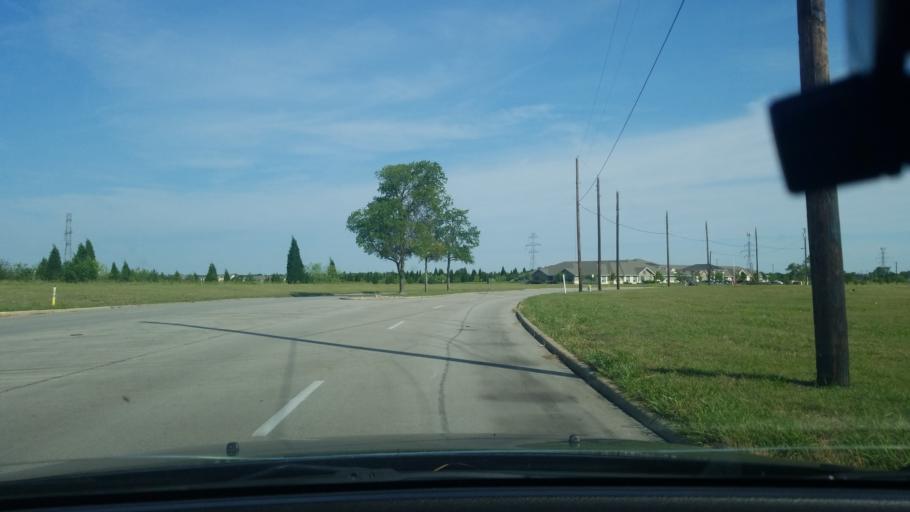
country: US
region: Texas
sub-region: Dallas County
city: Sunnyvale
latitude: 32.7809
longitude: -96.5700
